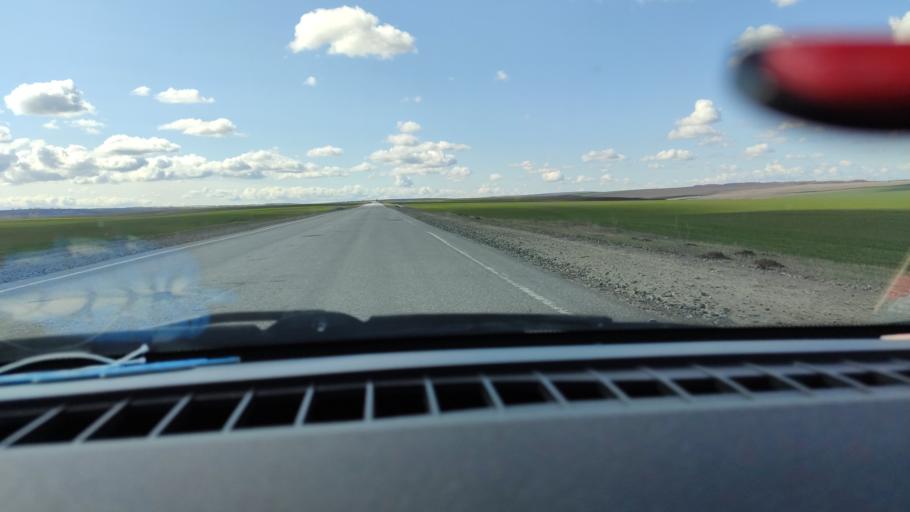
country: RU
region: Samara
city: Varlamovo
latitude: 53.0459
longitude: 48.3422
